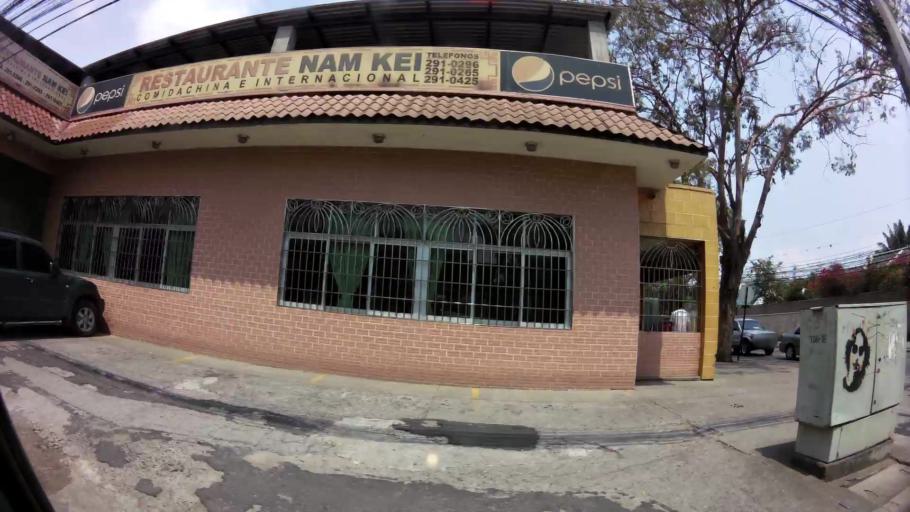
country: HN
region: Francisco Morazan
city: Tegucigalpa
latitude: 14.0537
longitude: -87.2291
